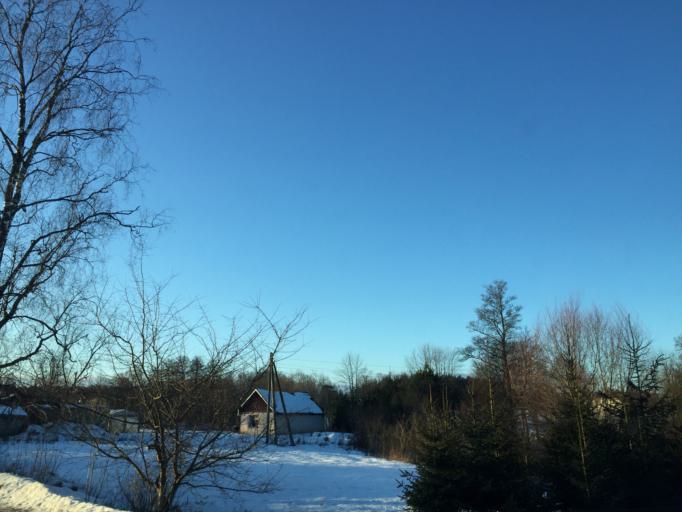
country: LV
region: Kegums
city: Kegums
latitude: 56.7448
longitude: 24.6670
